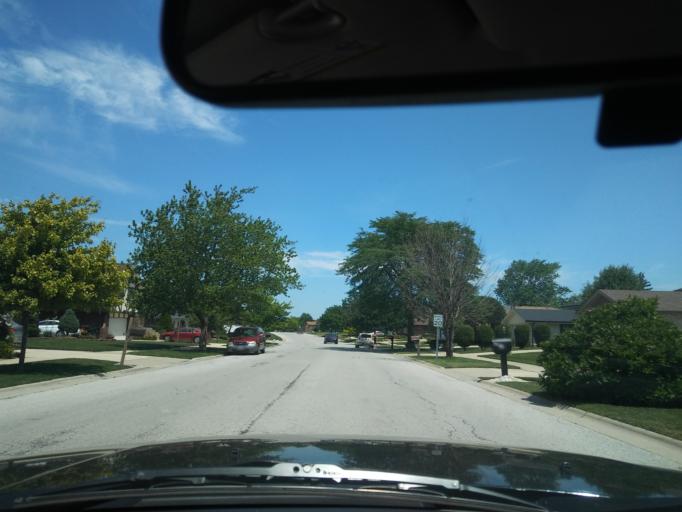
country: US
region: Illinois
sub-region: Cook County
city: Oak Forest
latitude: 41.6047
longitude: -87.7682
